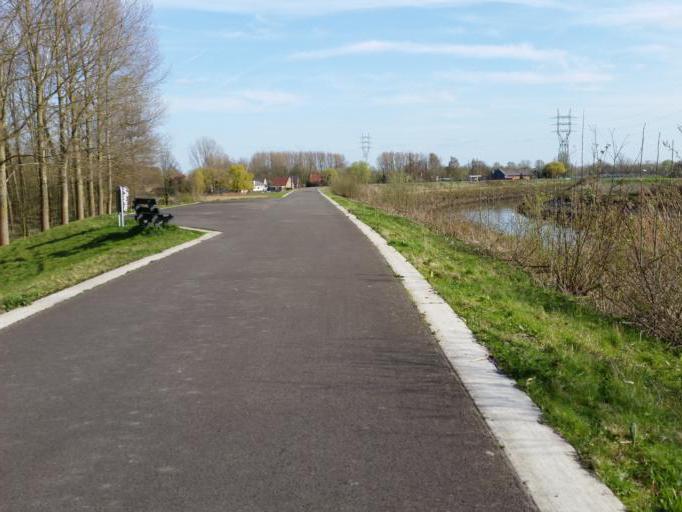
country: BE
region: Flanders
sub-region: Provincie Antwerpen
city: Rumst
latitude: 51.0388
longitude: 4.4199
